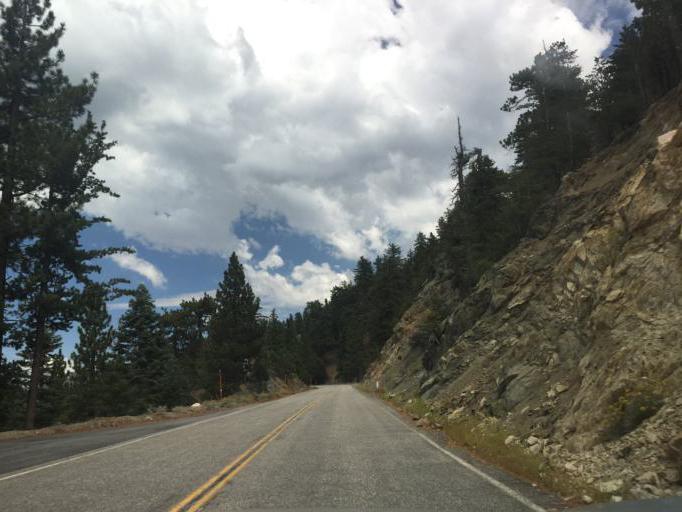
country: US
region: California
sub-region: Los Angeles County
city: Littlerock
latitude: 34.3472
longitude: -117.9076
